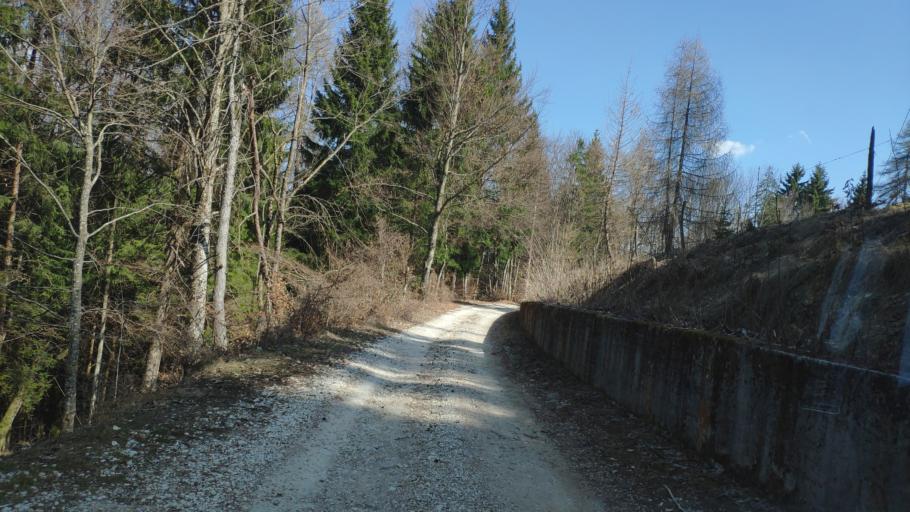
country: IT
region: Veneto
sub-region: Provincia di Vicenza
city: Enego
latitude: 45.9631
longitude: 11.6729
